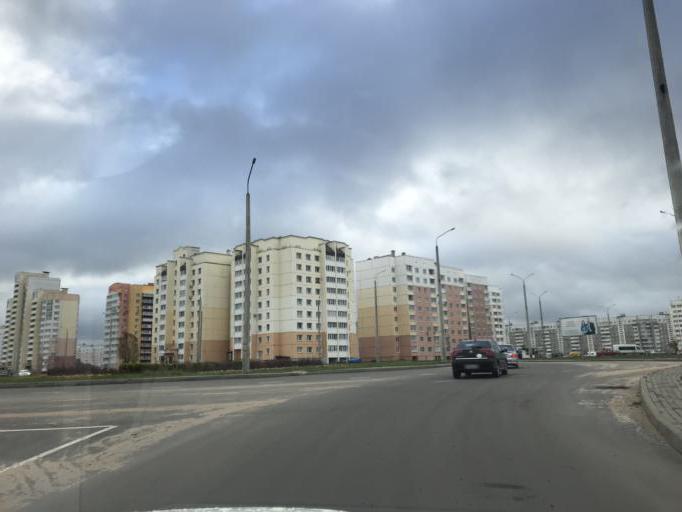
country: BY
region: Mogilev
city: Mahilyow
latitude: 53.8828
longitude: 30.3560
